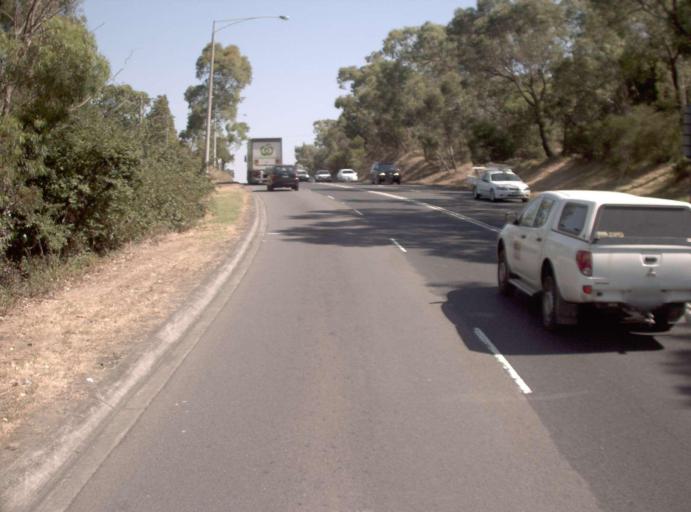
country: AU
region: Victoria
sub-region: Nillumbik
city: Eltham
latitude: -37.7347
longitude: 145.1349
